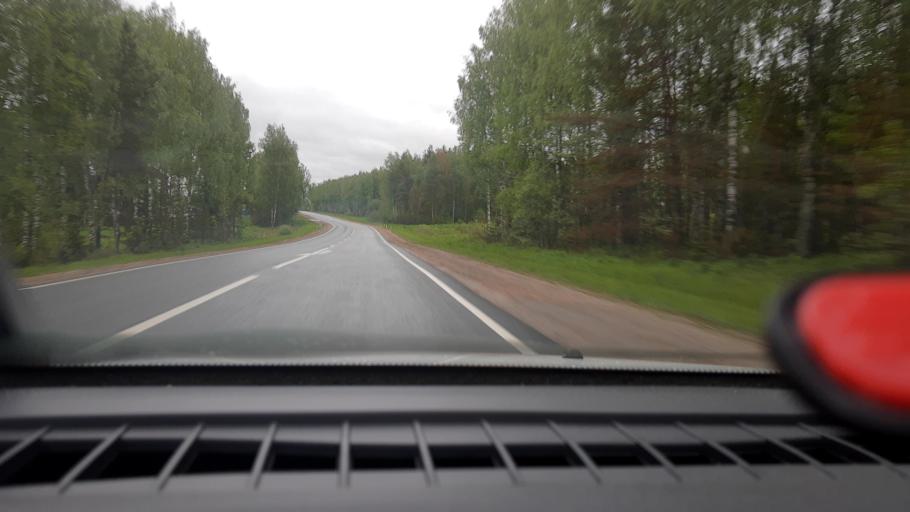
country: RU
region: Nizjnij Novgorod
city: Krasnyye Baki
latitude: 57.0517
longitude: 45.1360
